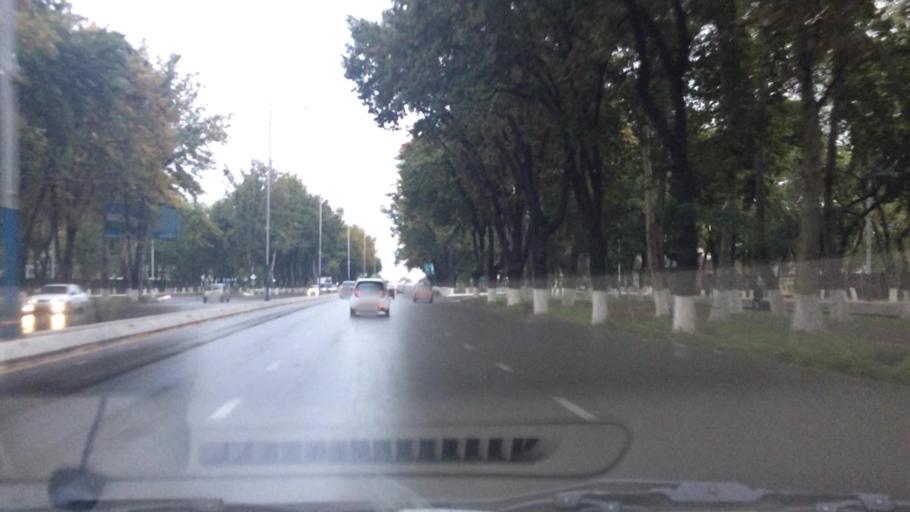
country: UZ
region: Toshkent Shahri
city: Tashkent
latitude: 41.2973
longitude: 69.2291
